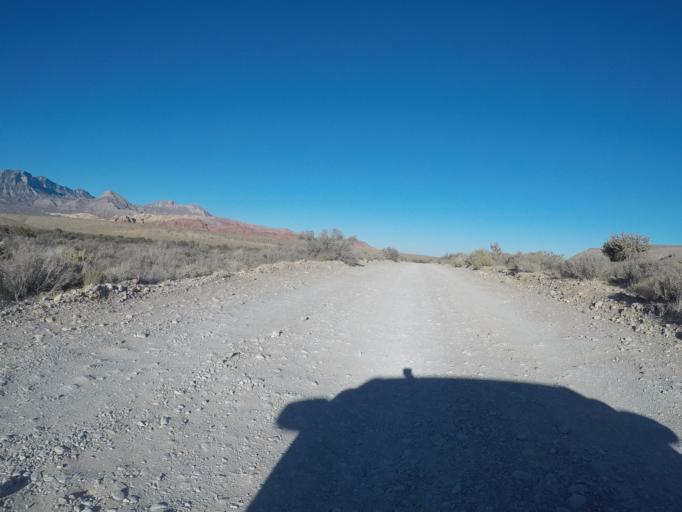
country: US
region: Nevada
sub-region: Clark County
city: Summerlin South
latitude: 36.1155
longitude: -115.4590
